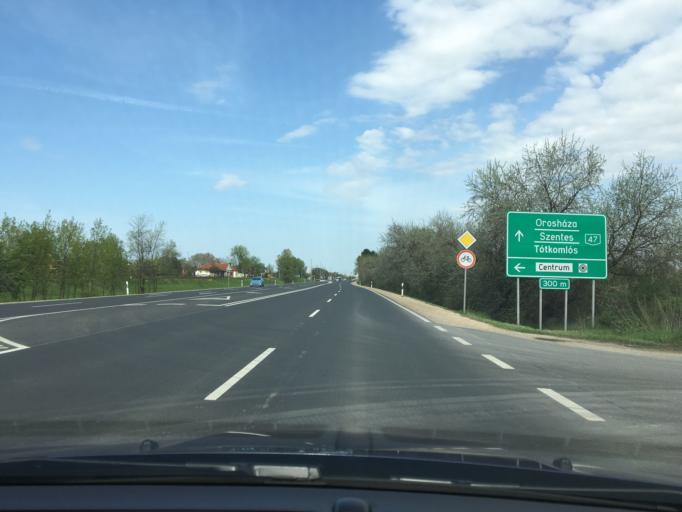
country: HU
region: Csongrad
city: Hodmezovasarhely
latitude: 46.4015
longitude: 20.3093
